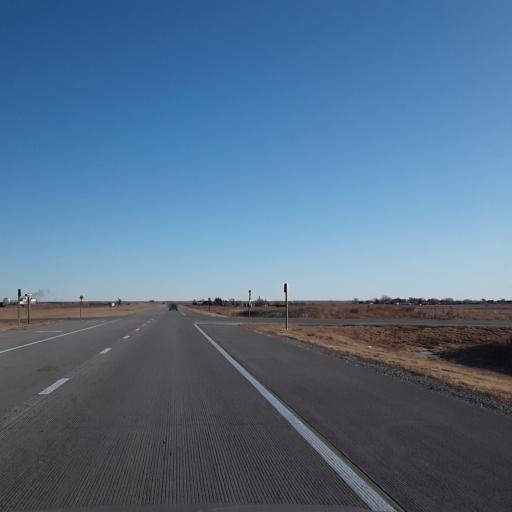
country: US
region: Kansas
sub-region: Seward County
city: Liberal
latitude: 37.0940
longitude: -100.8147
